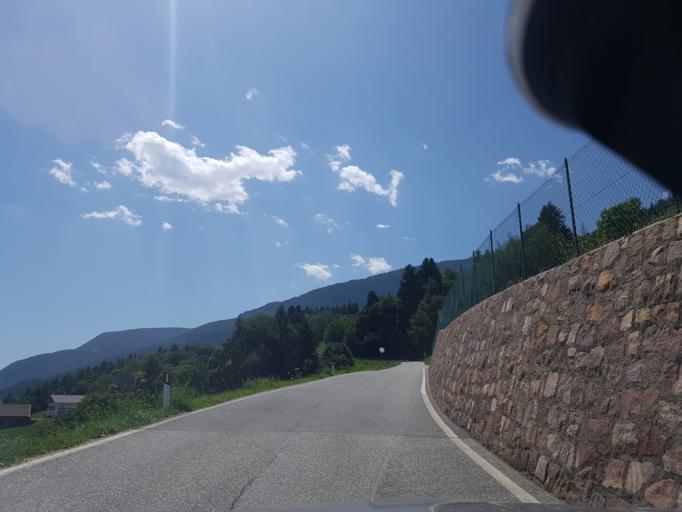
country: IT
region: Trentino-Alto Adige
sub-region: Bolzano
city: Villandro - Villanders
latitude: 46.6307
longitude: 11.5300
